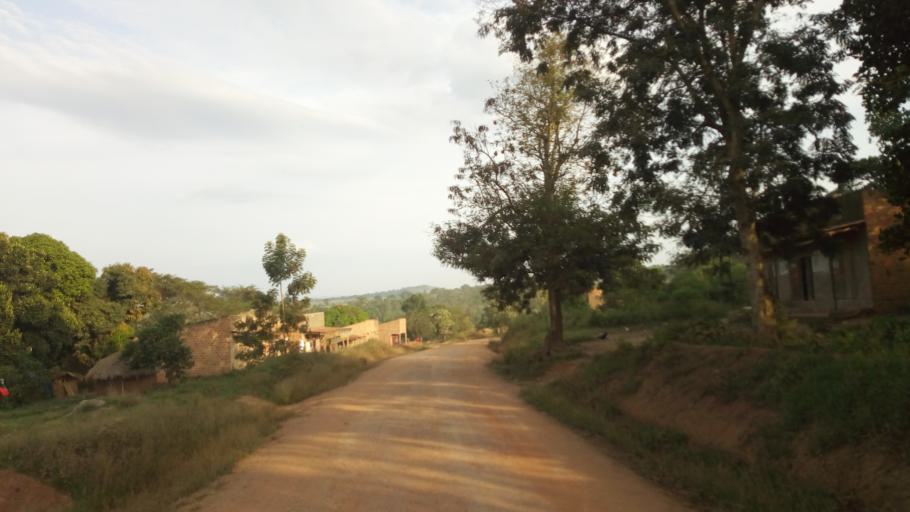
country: UG
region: Central Region
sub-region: Kiboga District
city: Kiboga
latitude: 0.6988
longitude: 31.7876
